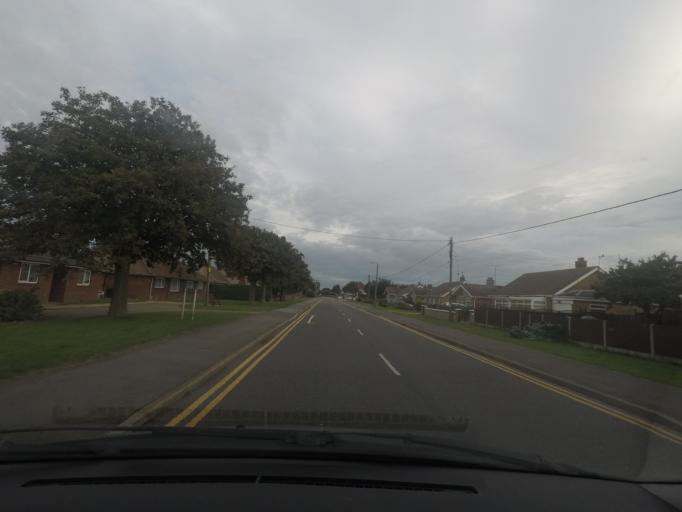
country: GB
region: England
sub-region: Lincolnshire
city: Chapel Saint Leonards
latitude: 53.2254
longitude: 0.3364
